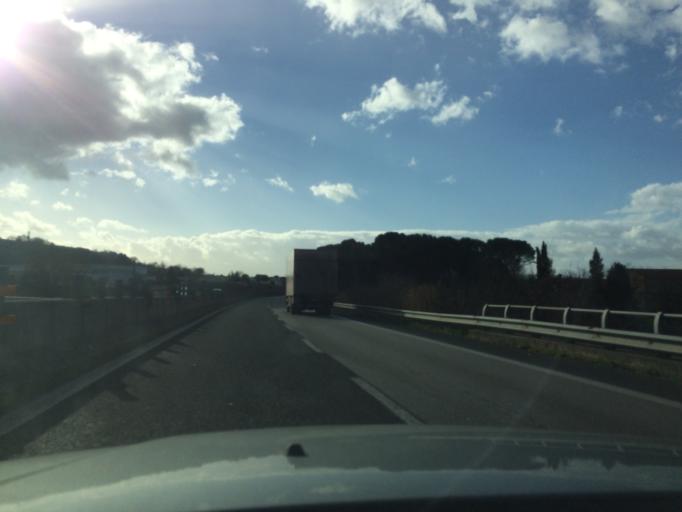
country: IT
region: Umbria
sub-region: Provincia di Perugia
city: Collepepe
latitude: 42.9109
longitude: 12.3921
